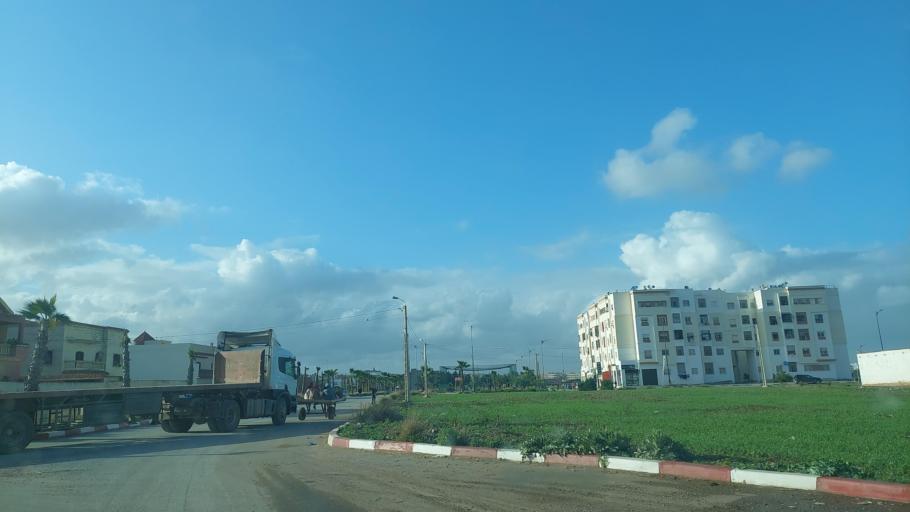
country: MA
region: Grand Casablanca
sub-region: Mediouna
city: Mediouna
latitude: 33.3739
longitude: -7.5264
